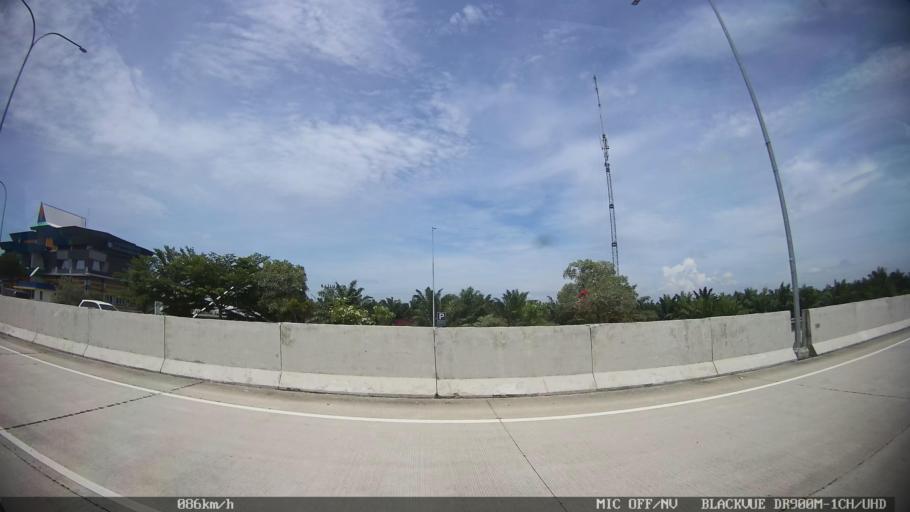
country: ID
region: North Sumatra
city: Percut
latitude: 3.5898
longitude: 98.8448
